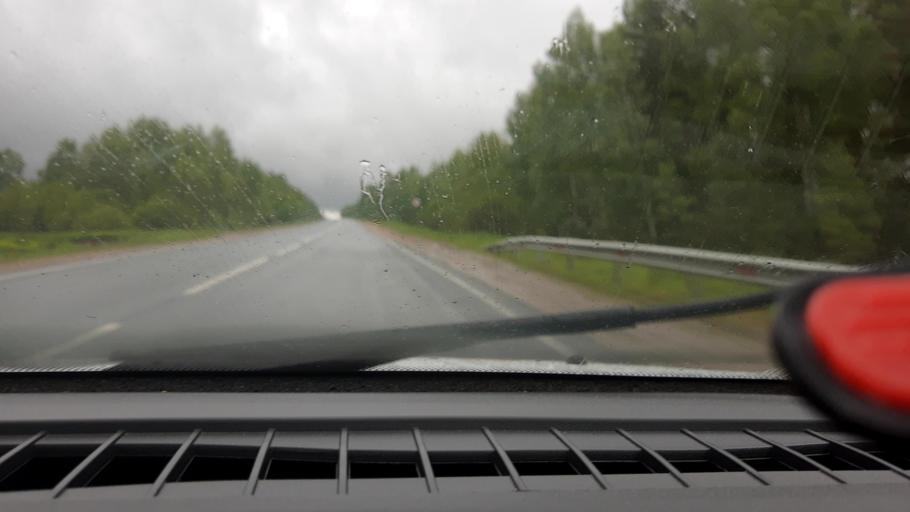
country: RU
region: Nizjnij Novgorod
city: Semenov
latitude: 56.7733
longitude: 44.4215
